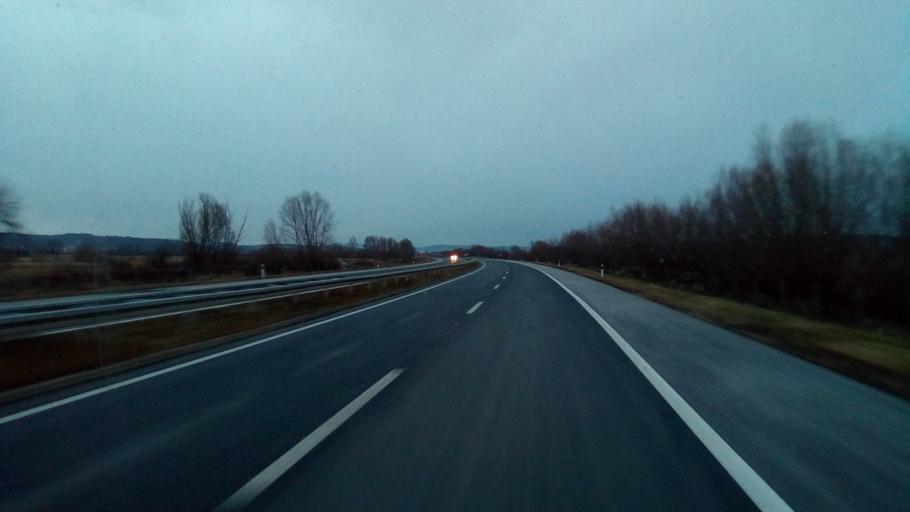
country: HR
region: Zagrebacka
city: Brckovljani
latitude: 45.9596
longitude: 16.2825
